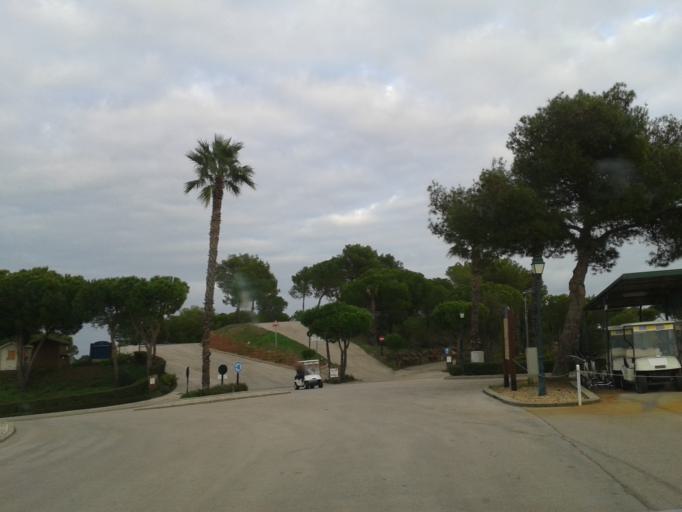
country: PT
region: Faro
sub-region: Castro Marim
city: Castro Marim
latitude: 37.2361
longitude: -7.4697
